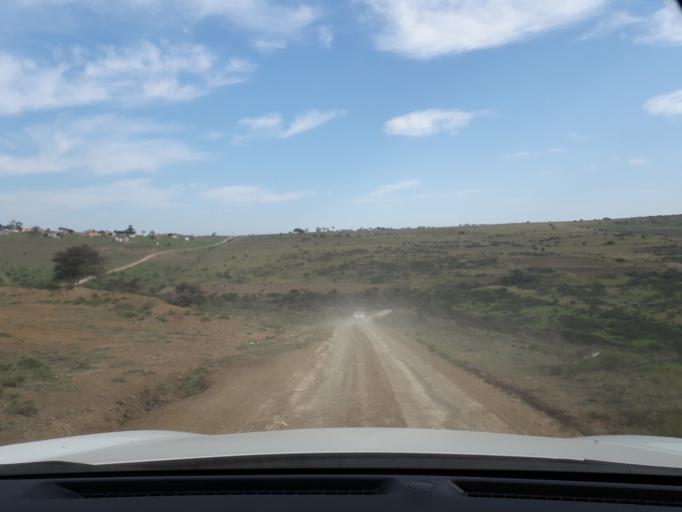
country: ZA
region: Eastern Cape
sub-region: Buffalo City Metropolitan Municipality
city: Bhisho
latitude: -32.9948
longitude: 27.3399
